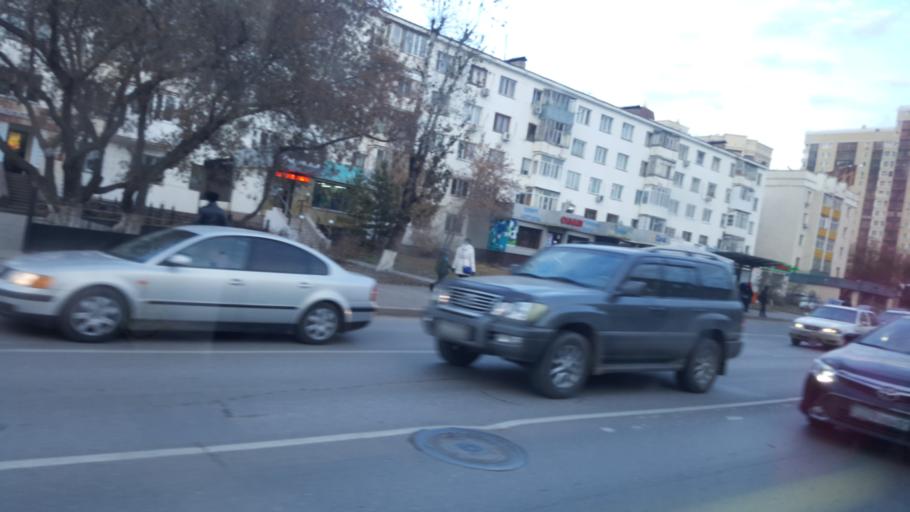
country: KZ
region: Astana Qalasy
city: Astana
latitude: 51.1666
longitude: 71.4373
